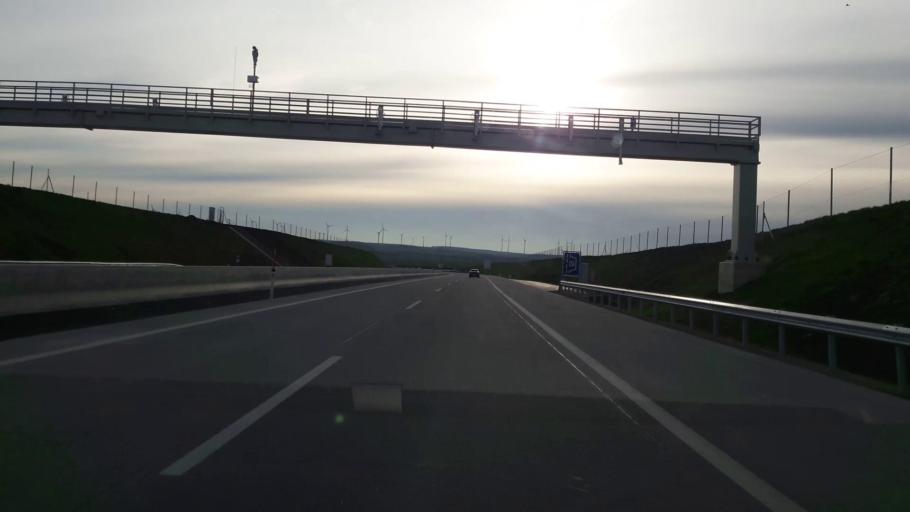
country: AT
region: Lower Austria
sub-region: Politischer Bezirk Mistelbach
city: Wilfersdorf
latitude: 48.5857
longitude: 16.6268
